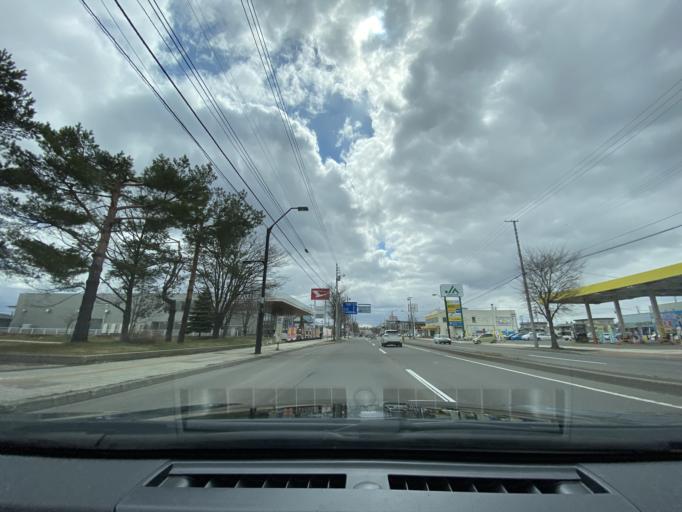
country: JP
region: Hokkaido
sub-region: Asahikawa-shi
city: Asahikawa
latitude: 43.7567
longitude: 142.3507
